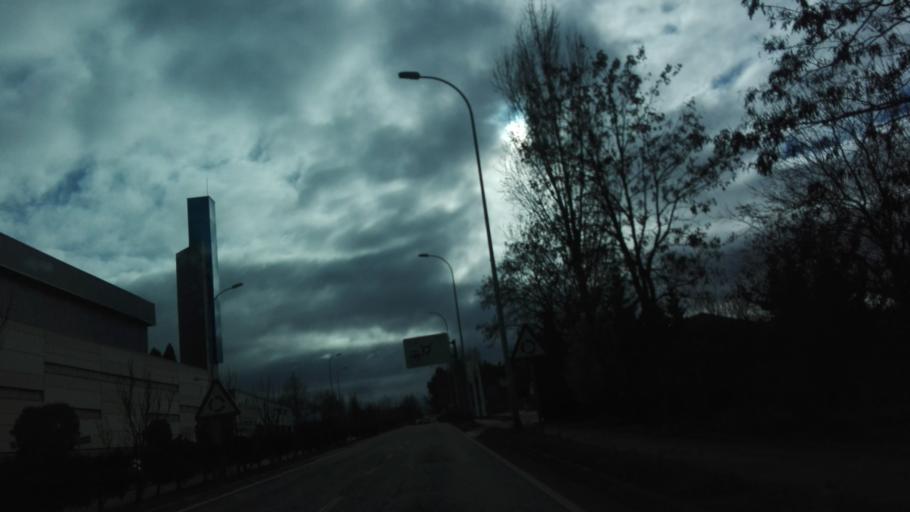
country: ES
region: Navarre
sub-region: Provincia de Navarra
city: Egues-Uharte
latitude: 42.8278
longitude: -1.5849
